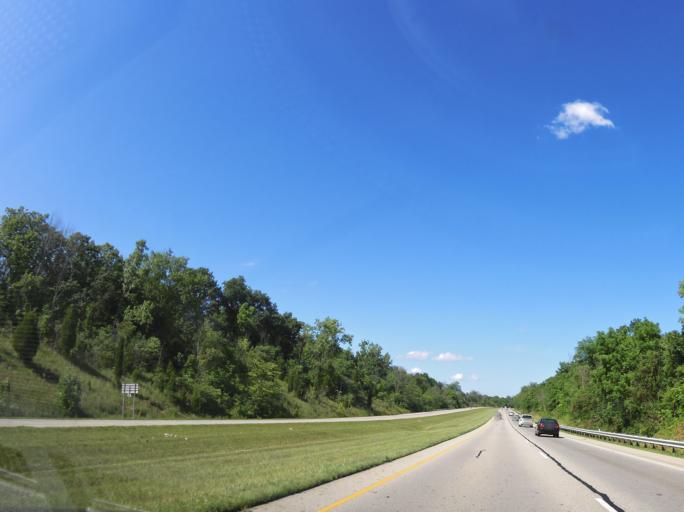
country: US
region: Ohio
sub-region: Greene County
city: Wright-Patterson AFB
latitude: 39.8077
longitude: -84.0918
